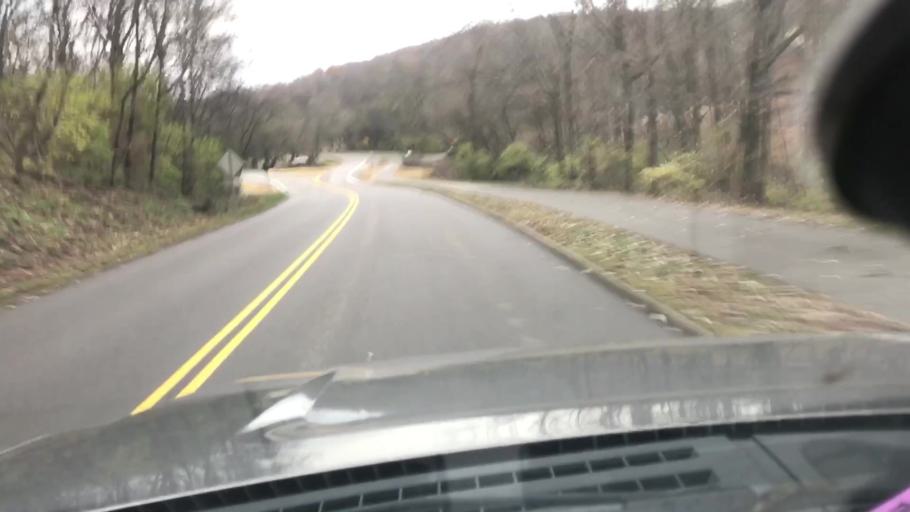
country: US
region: Tennessee
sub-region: Williamson County
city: Brentwood Estates
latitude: 35.9687
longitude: -86.7549
